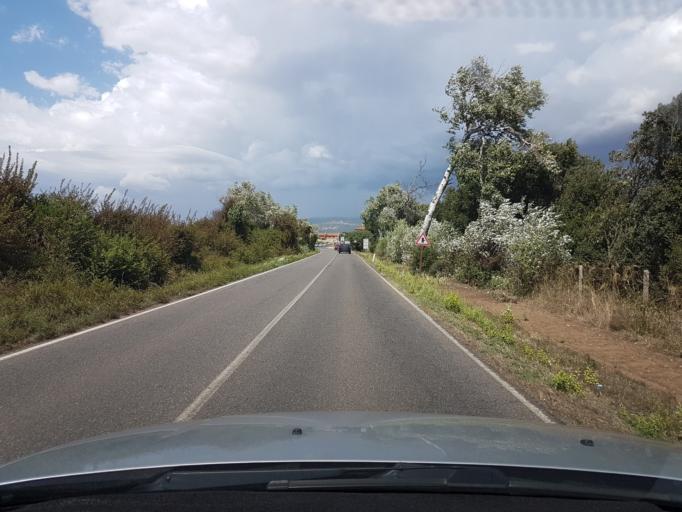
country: IT
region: Sardinia
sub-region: Provincia di Oristano
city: Riola Sardo
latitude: 39.9861
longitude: 8.5403
